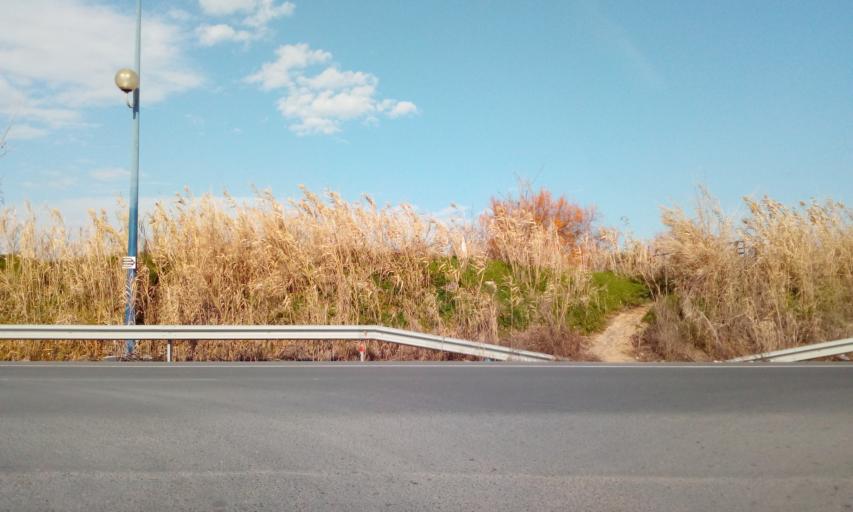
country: ES
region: Andalusia
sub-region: Provincia de Huelva
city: Lepe
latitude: 37.2104
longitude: -7.2034
